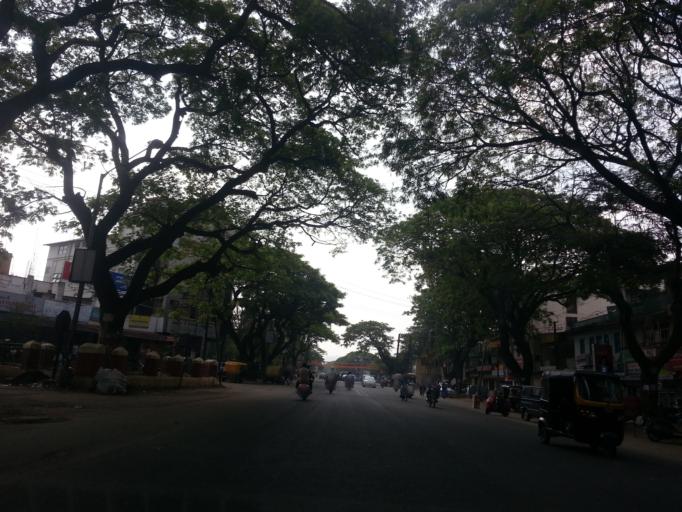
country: IN
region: Karnataka
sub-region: Mysore
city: Mysore
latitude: 12.3213
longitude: 76.6468
